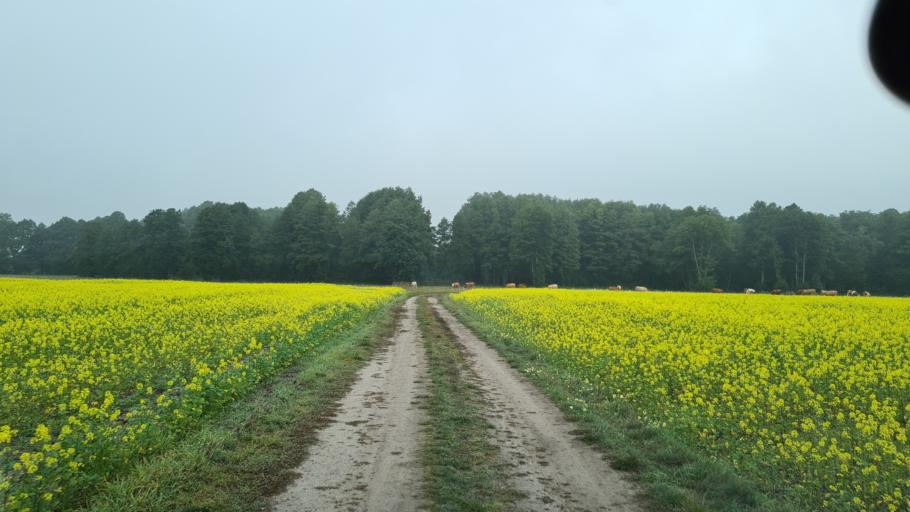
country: DE
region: Brandenburg
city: Schonewalde
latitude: 51.6572
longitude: 13.6091
